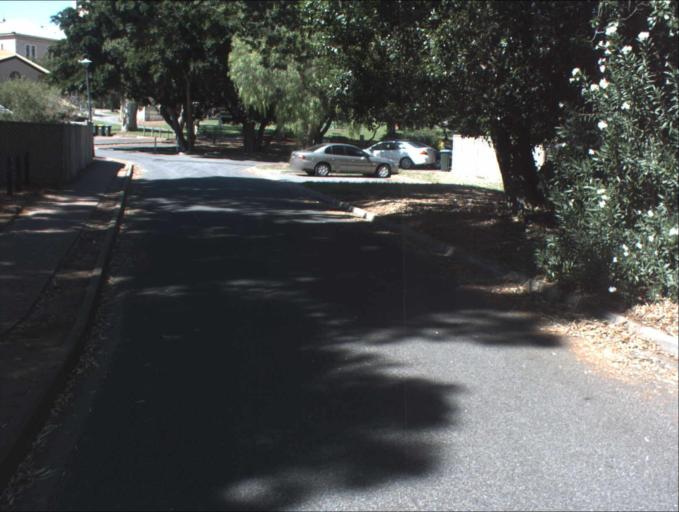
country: AU
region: South Australia
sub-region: Port Adelaide Enfield
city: Blair Athol
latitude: -34.8642
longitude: 138.6059
